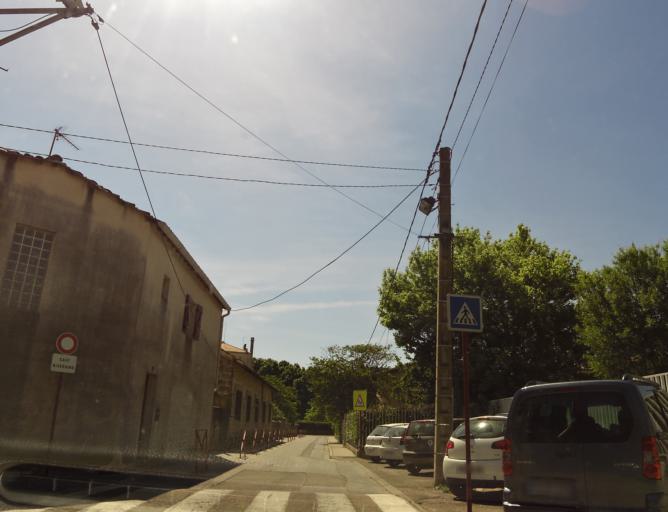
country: FR
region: Languedoc-Roussillon
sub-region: Departement du Gard
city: Sommieres
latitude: 43.7867
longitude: 4.0889
